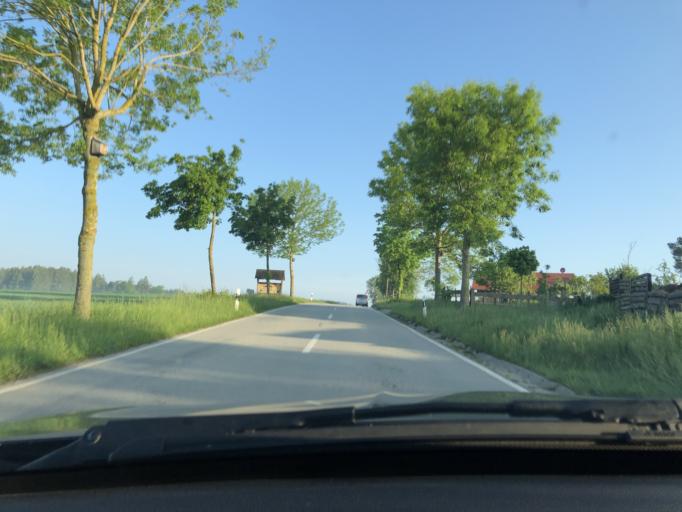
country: DE
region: Bavaria
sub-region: Upper Bavaria
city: Kirchdorf
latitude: 48.4766
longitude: 11.6348
